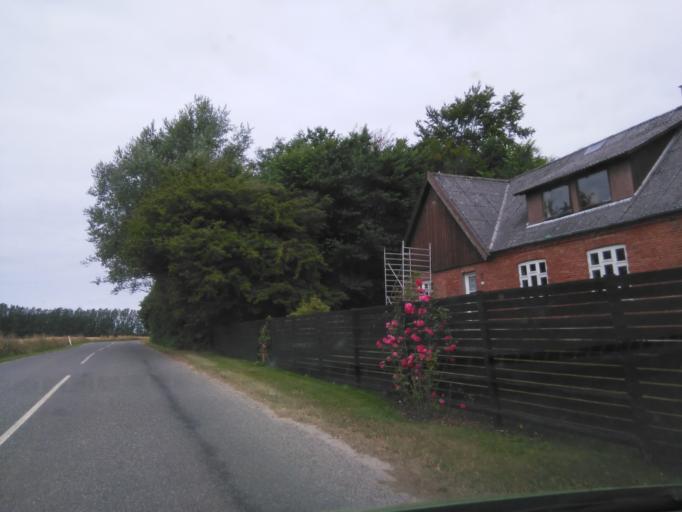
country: DK
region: Central Jutland
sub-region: Arhus Kommune
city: Solbjerg
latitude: 56.0330
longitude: 10.1224
